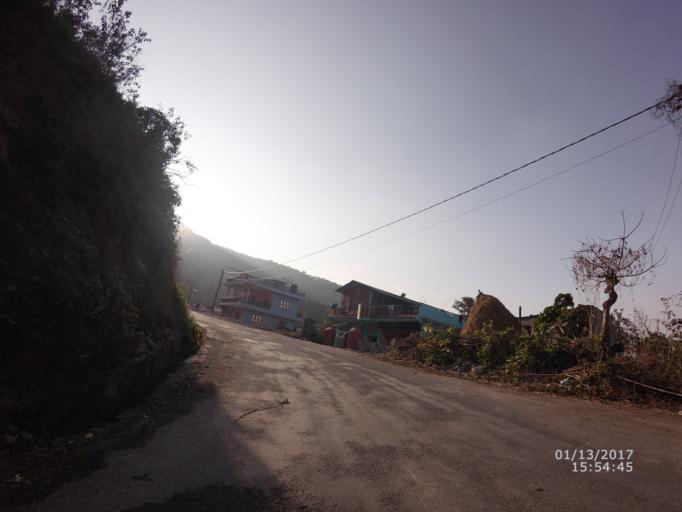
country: NP
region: Western Region
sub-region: Gandaki Zone
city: Pokhara
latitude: 28.1603
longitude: 84.0083
